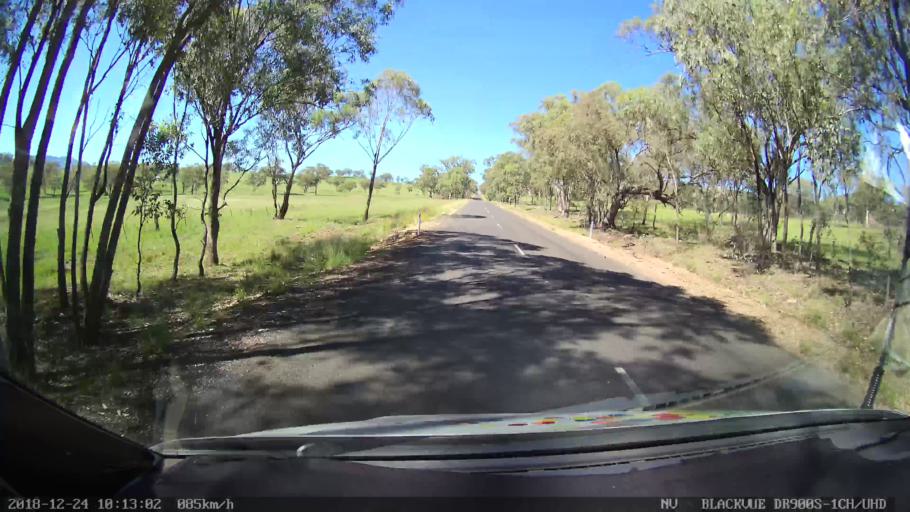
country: AU
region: New South Wales
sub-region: Liverpool Plains
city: Quirindi
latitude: -31.6855
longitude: 150.6428
